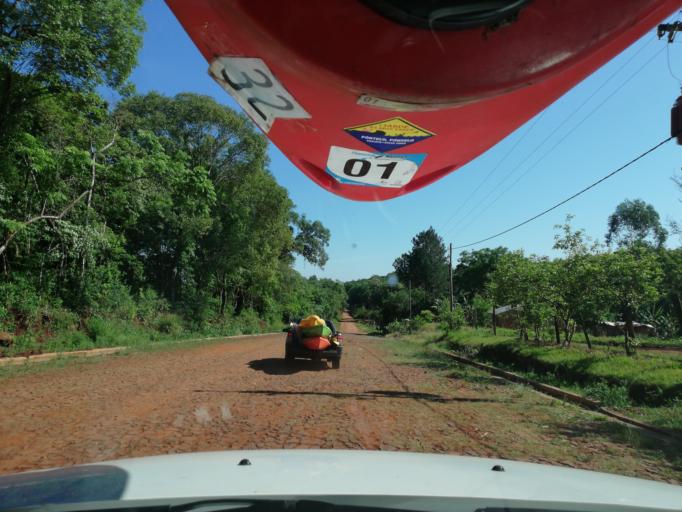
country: AR
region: Misiones
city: Puerto Leoni
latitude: -26.9814
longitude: -55.1648
